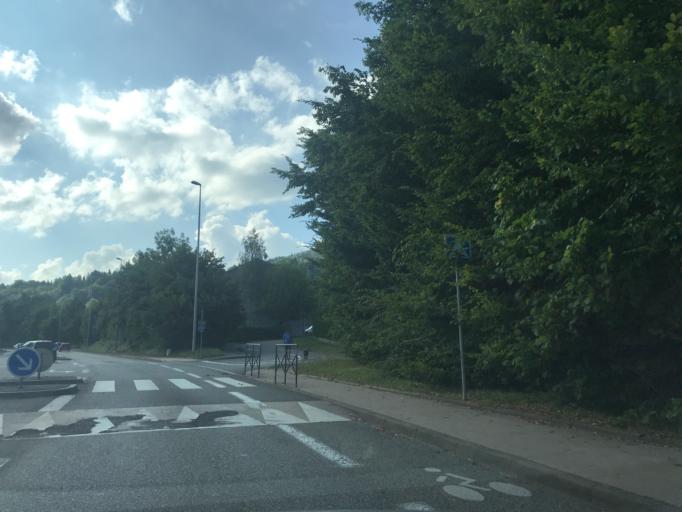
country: FR
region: Rhone-Alpes
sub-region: Departement de la Haute-Savoie
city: Villaz
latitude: 45.9222
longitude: 6.1758
